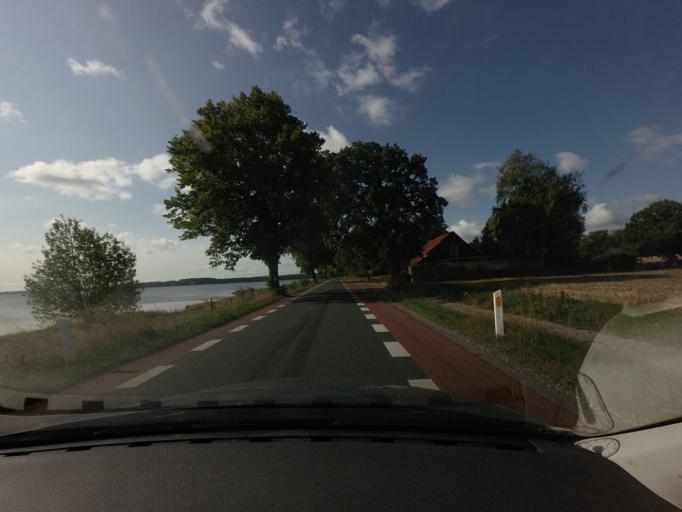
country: DK
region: Zealand
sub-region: Vordingborg Kommune
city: Praesto
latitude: 55.1593
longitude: 12.0201
